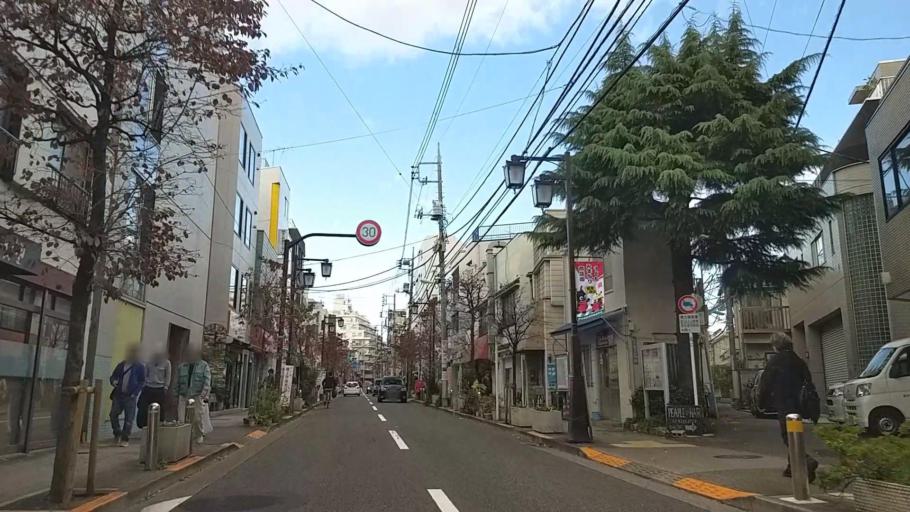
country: JP
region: Tokyo
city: Tokyo
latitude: 35.6482
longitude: 139.6686
